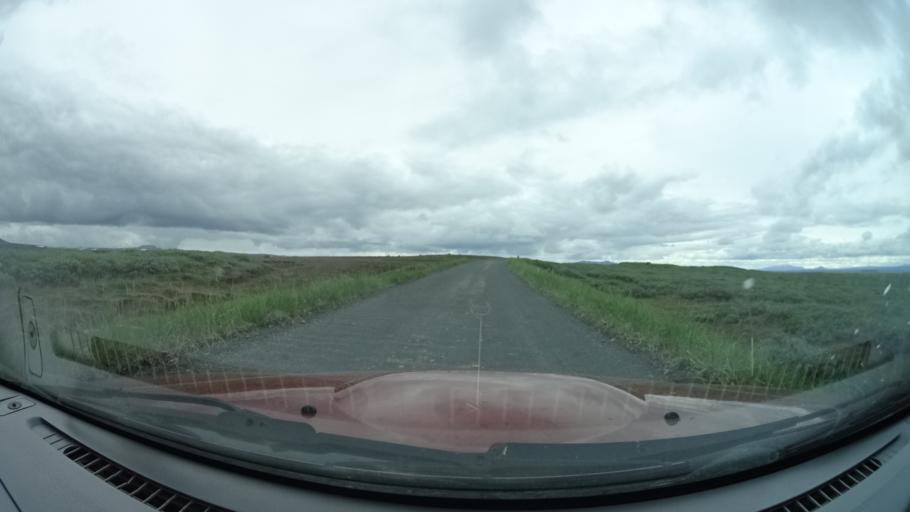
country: IS
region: Northeast
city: Laugar
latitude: 65.6768
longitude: -16.1689
